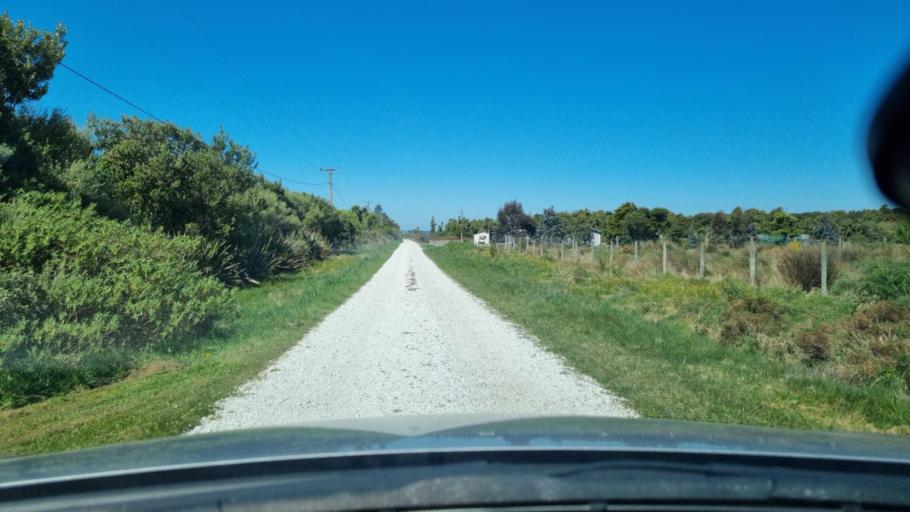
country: NZ
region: Southland
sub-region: Invercargill City
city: Invercargill
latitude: -46.4508
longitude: 168.3167
